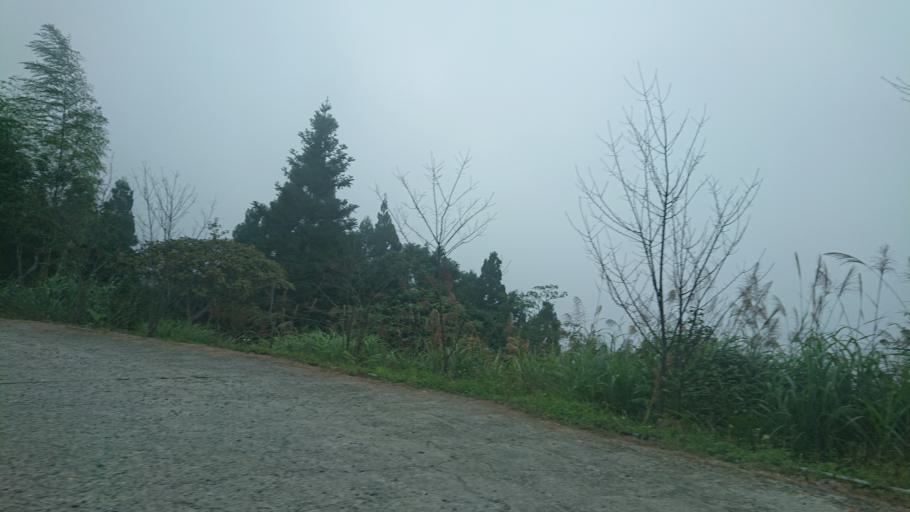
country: TW
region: Taiwan
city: Lugu
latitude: 23.6263
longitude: 120.7110
